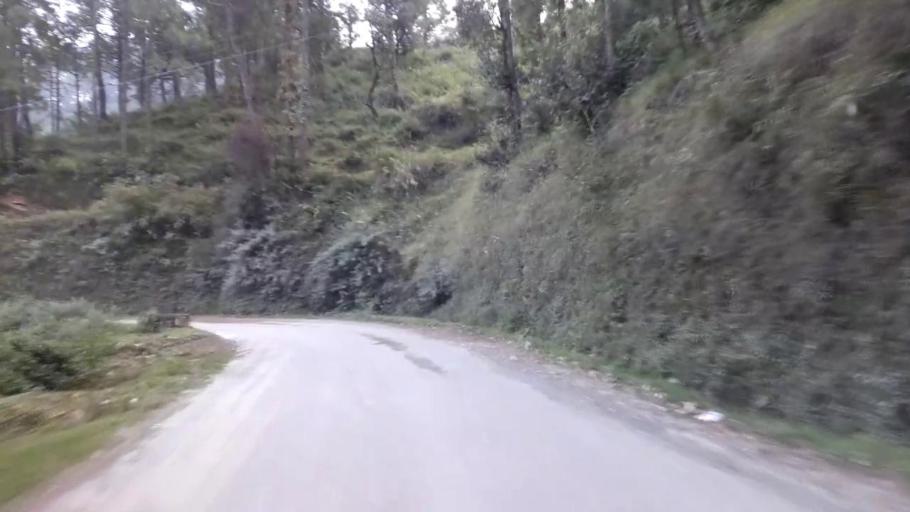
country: IN
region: Himachal Pradesh
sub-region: Shimla
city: Shimla
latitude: 31.0664
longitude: 77.1479
